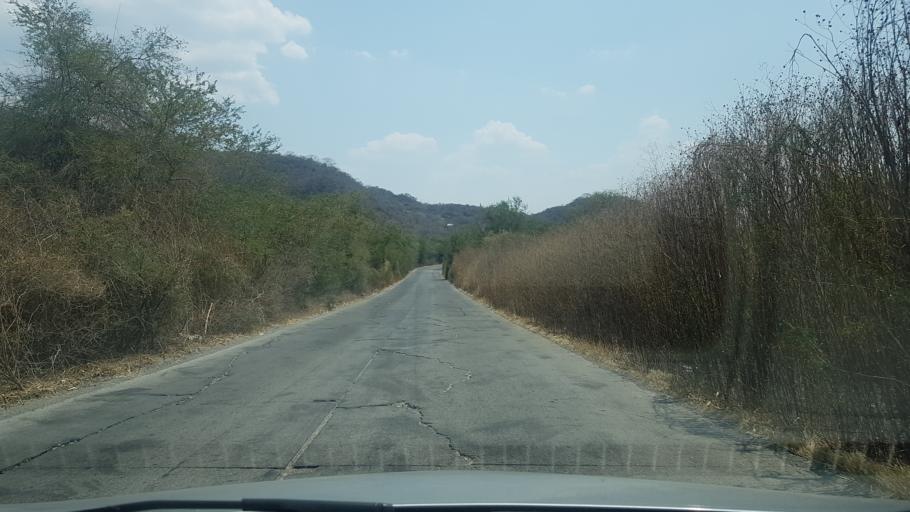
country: MX
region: Morelos
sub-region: Tlaltizapan de Zapata
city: Colonia Palo Prieto (Chipitongo)
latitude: 18.7608
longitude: -99.1082
